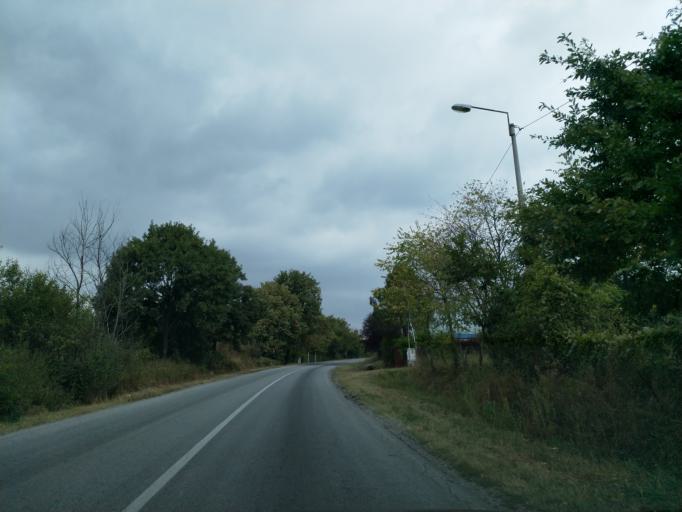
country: RS
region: Central Serbia
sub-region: Pomoravski Okrug
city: Jagodina
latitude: 44.0076
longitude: 21.2036
